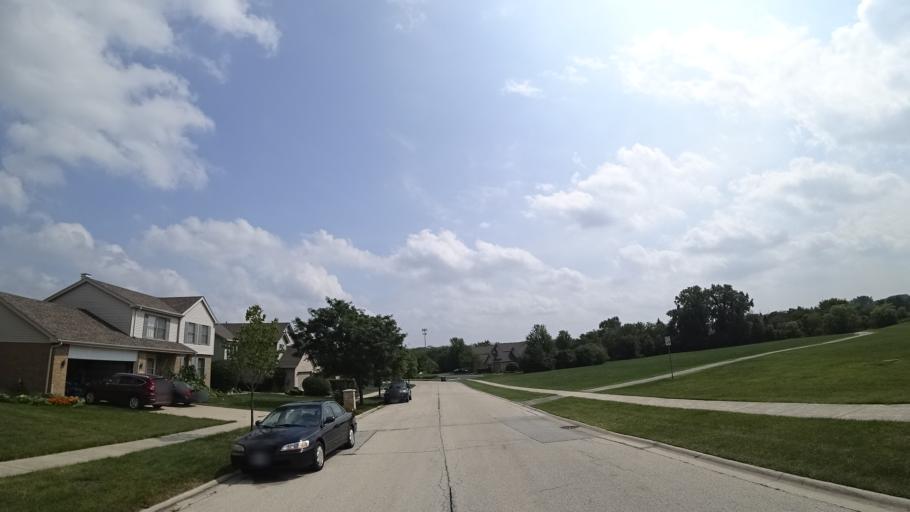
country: US
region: Illinois
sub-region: Will County
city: Goodings Grove
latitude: 41.6329
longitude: -87.8949
